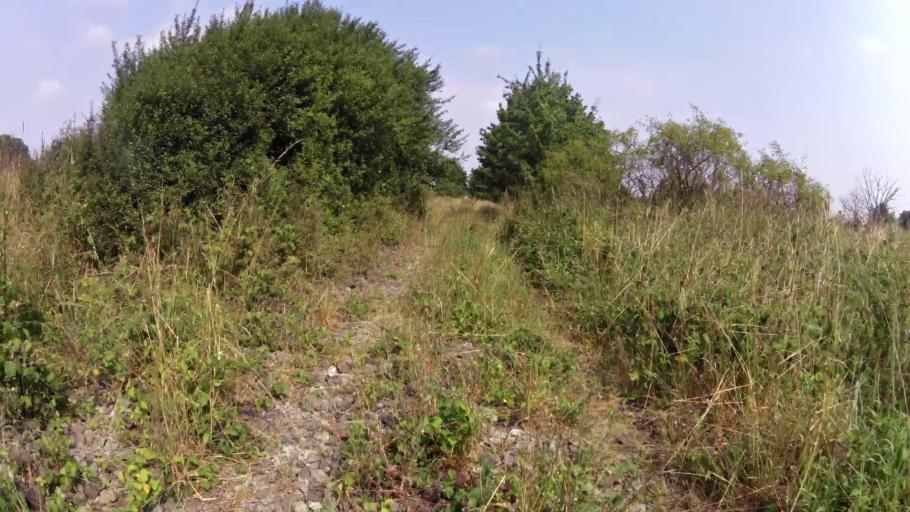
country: PL
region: West Pomeranian Voivodeship
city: Trzcinsko Zdroj
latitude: 52.9305
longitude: 14.5609
